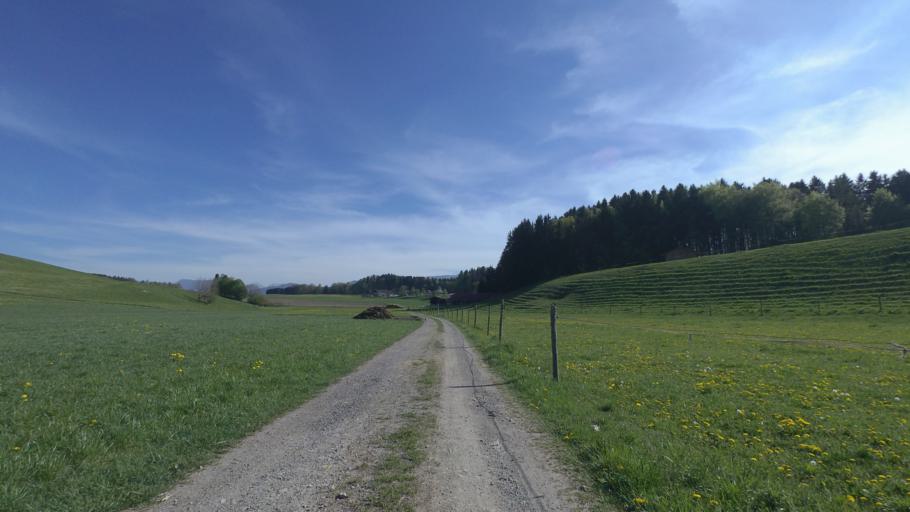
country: DE
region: Bavaria
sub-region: Upper Bavaria
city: Grabenstatt
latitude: 47.8656
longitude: 12.5700
